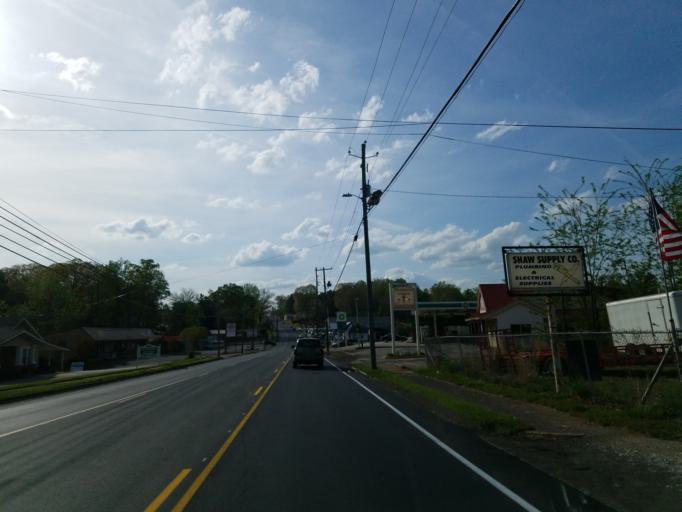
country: US
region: Georgia
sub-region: Pickens County
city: Jasper
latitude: 34.4655
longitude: -84.4197
